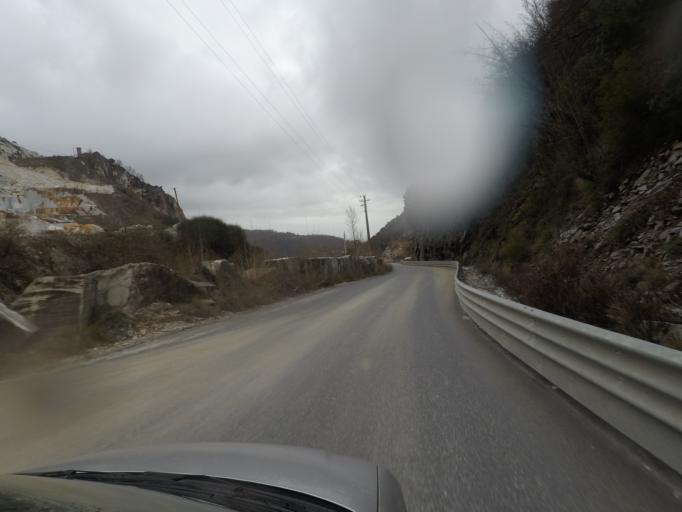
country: IT
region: Tuscany
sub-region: Provincia di Massa-Carrara
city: Massa
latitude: 44.0873
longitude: 10.1298
